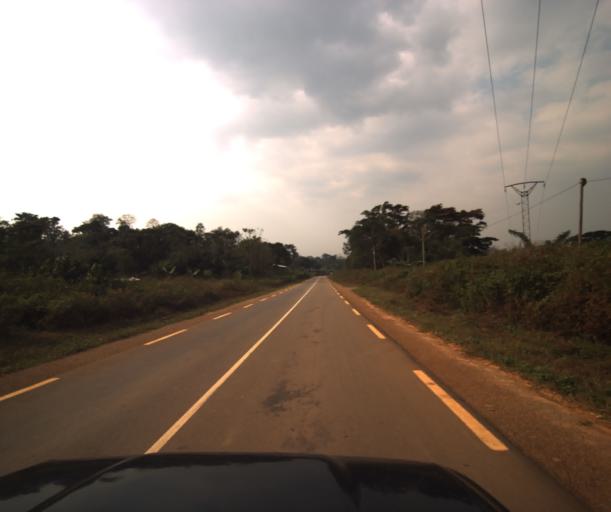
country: CM
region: Centre
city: Mbankomo
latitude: 3.7597
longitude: 11.4060
